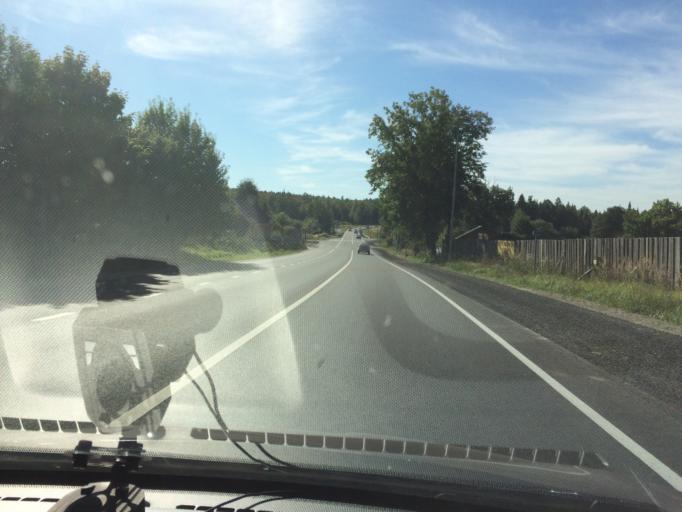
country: RU
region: Mariy-El
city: Yoshkar-Ola
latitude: 56.6000
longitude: 47.9712
